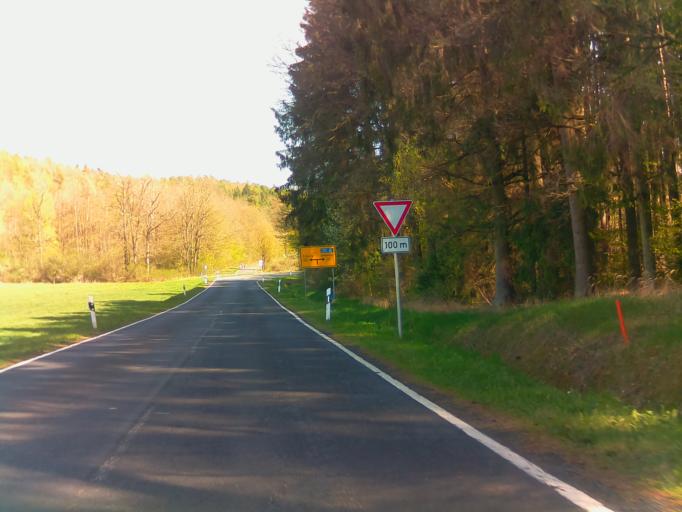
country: DE
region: Bavaria
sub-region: Regierungsbezirk Unterfranken
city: Burgpreppach
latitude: 50.1367
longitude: 10.5937
